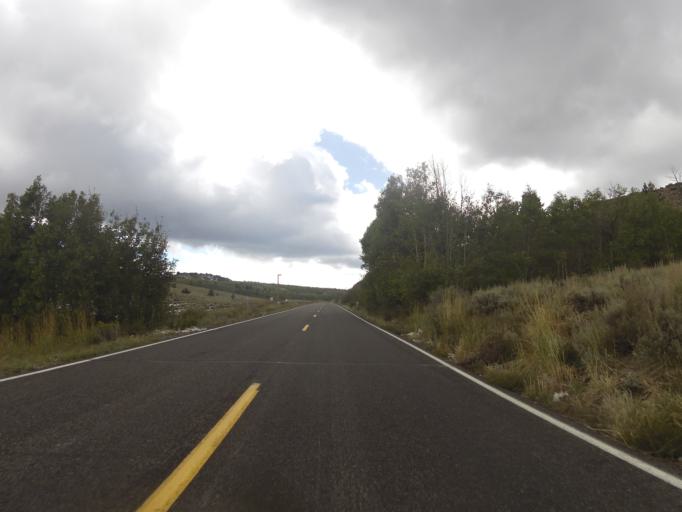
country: US
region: Nevada
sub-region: Douglas County
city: Gardnerville Ranchos
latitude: 38.6796
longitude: -119.5988
